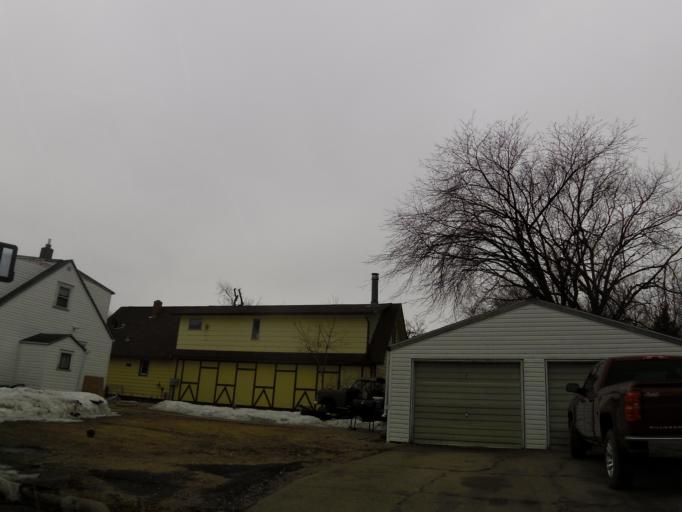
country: US
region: North Dakota
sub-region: Walsh County
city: Grafton
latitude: 48.4155
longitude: -97.4208
